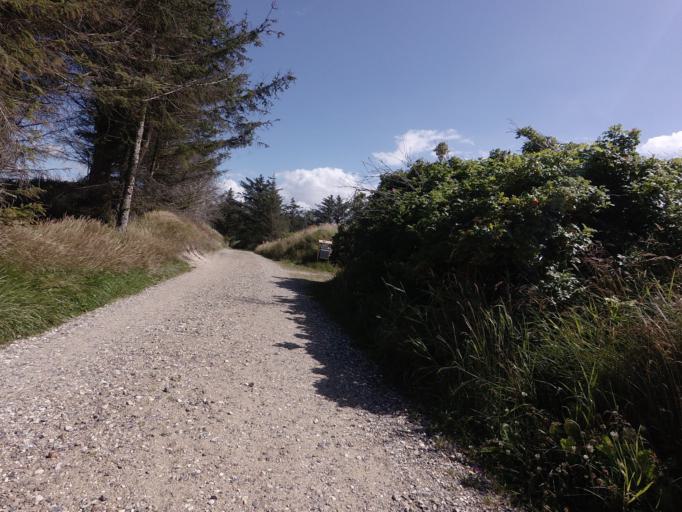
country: DK
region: North Denmark
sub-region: Jammerbugt Kommune
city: Pandrup
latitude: 57.3041
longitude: 9.6479
